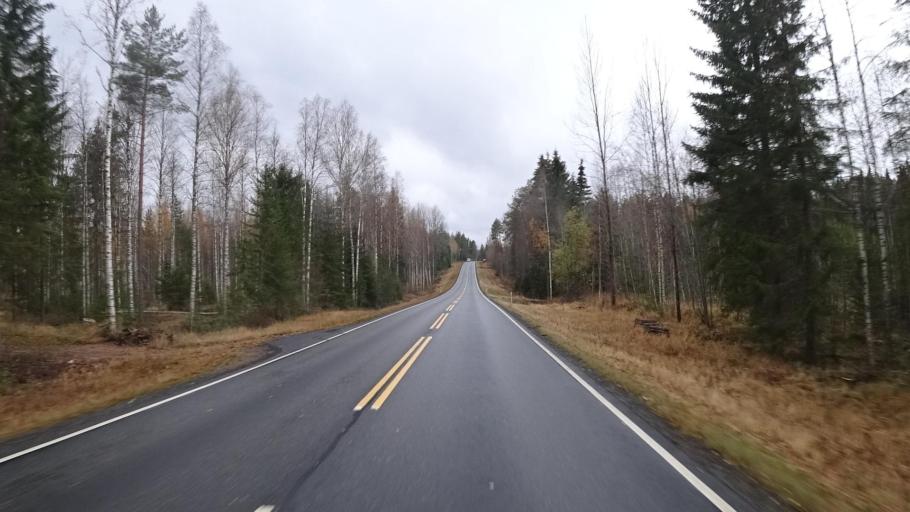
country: FI
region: Southern Savonia
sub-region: Mikkeli
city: Kangasniemi
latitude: 62.1693
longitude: 26.8515
